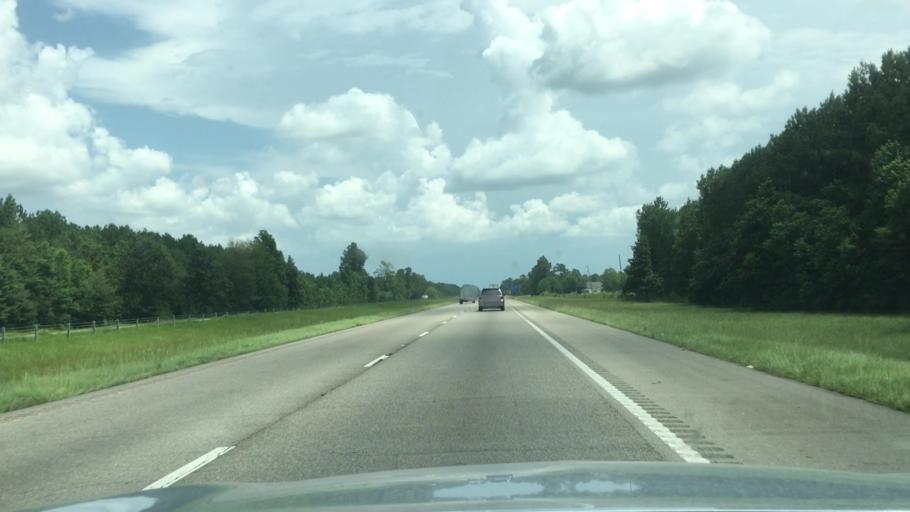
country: US
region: Mississippi
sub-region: Pearl River County
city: Nicholson
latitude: 30.4881
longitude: -89.6732
